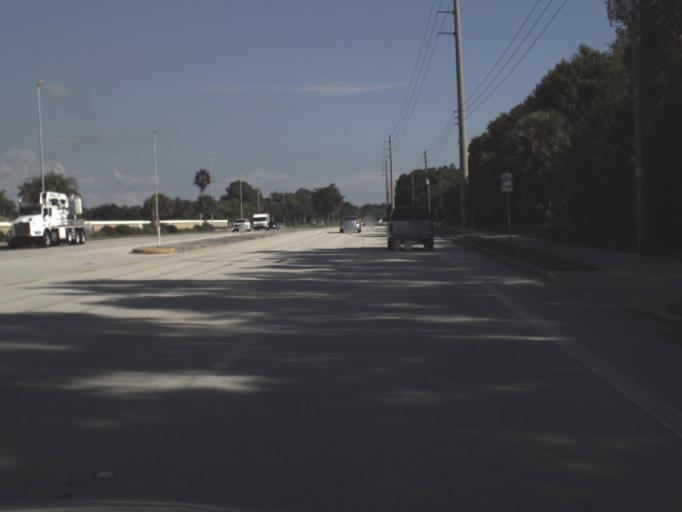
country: US
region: Florida
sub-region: Sarasota County
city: South Venice
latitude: 27.0260
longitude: -82.3966
